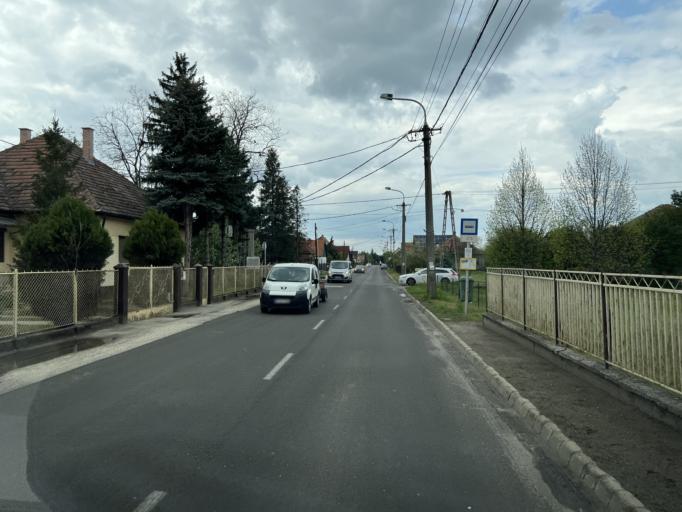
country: HU
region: Pest
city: Hernad
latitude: 47.1670
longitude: 19.4235
